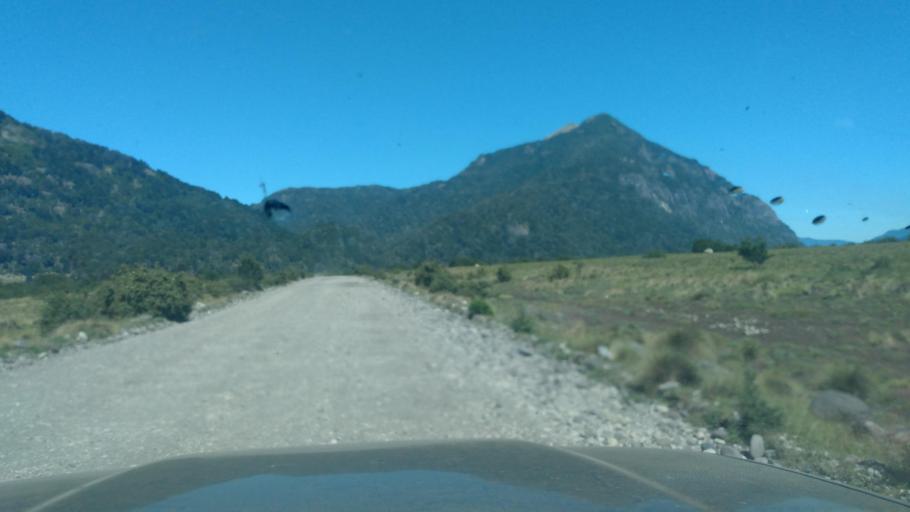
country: AR
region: Neuquen
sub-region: Departamento de Lacar
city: San Martin de los Andes
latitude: -39.7458
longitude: -71.5099
